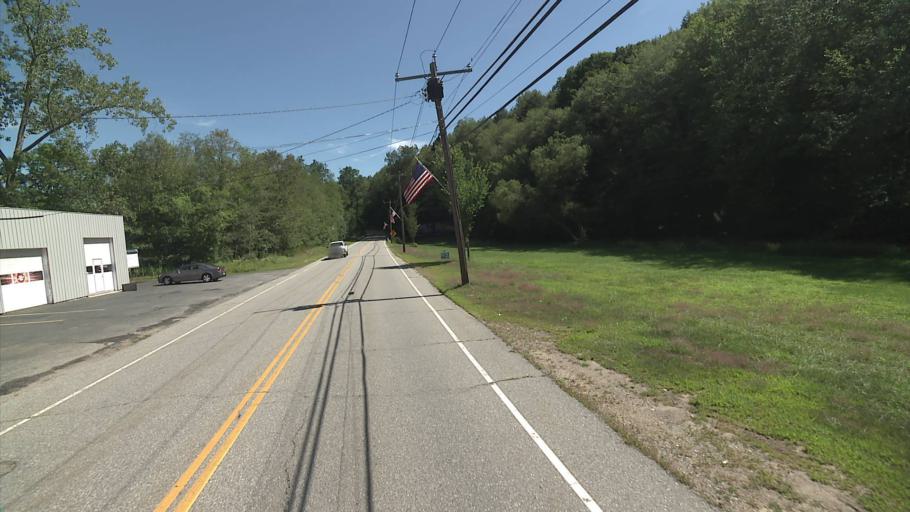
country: US
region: Connecticut
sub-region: New London County
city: Baltic
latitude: 41.6114
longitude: -72.0733
